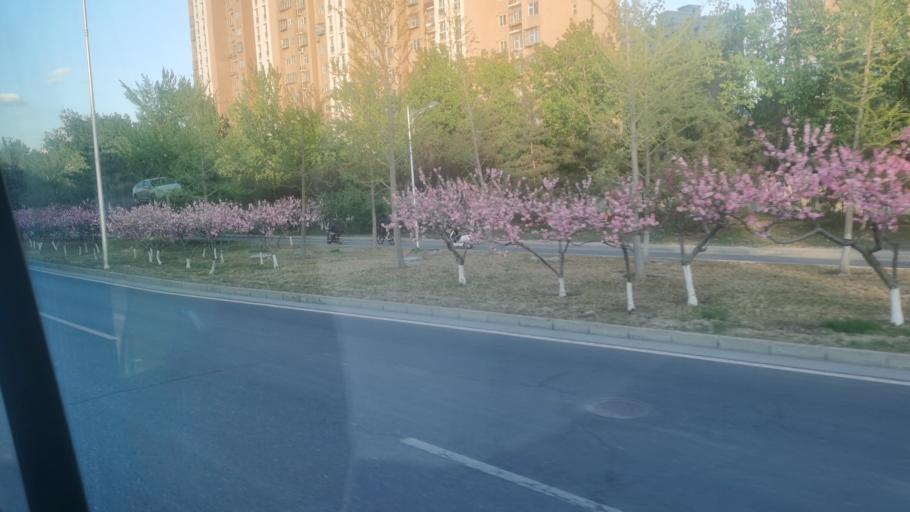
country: CN
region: Beijing
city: Xibeiwang
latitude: 40.0777
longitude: 116.2551
